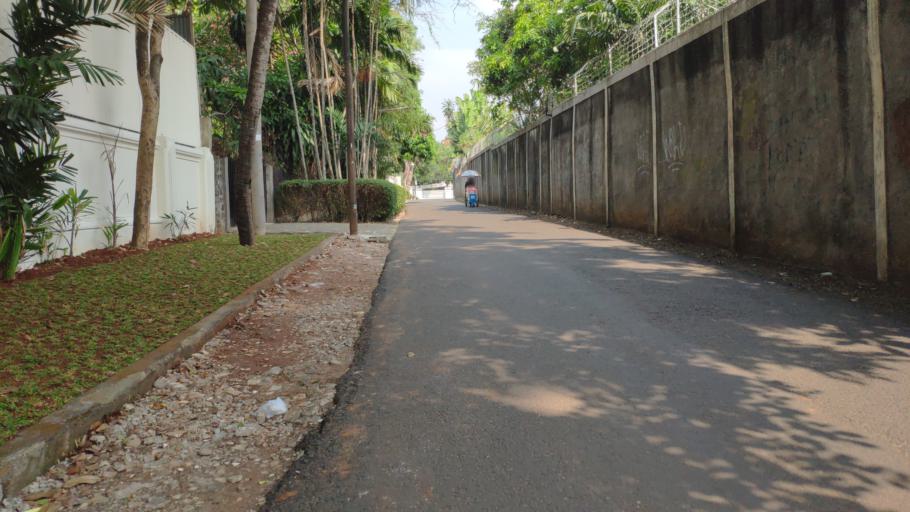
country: ID
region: Jakarta Raya
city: Jakarta
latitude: -6.2734
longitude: 106.8229
